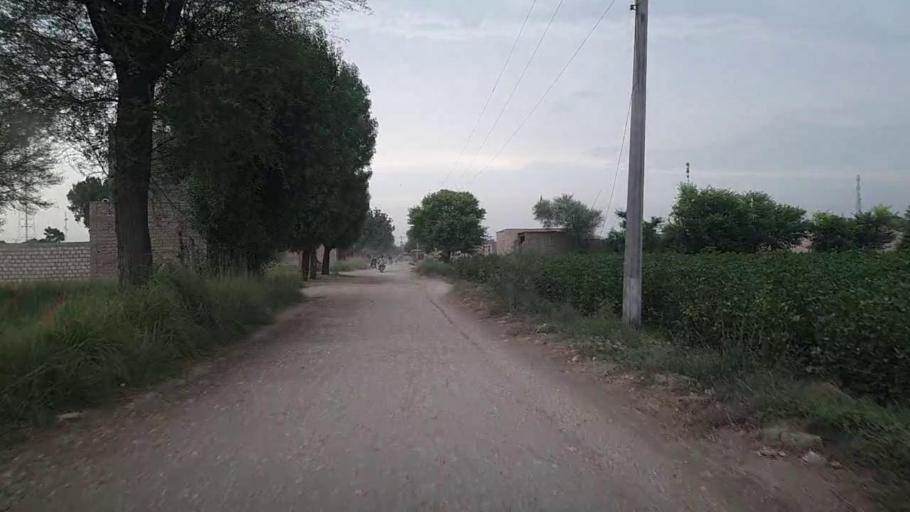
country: PK
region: Sindh
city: Karaundi
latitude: 26.9849
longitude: 68.3438
